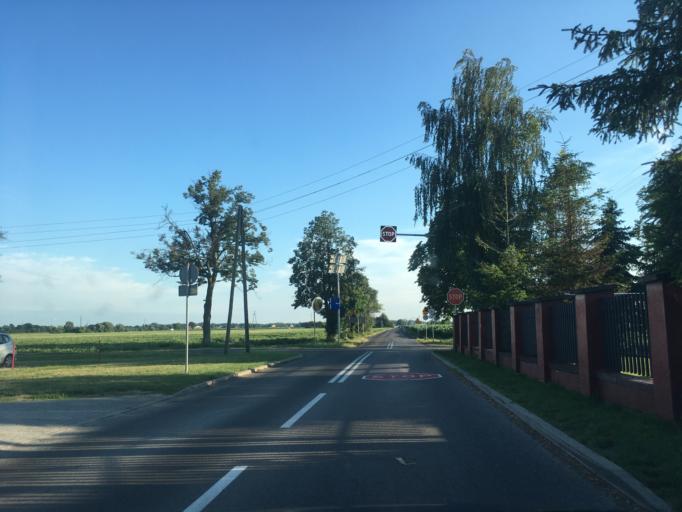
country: PL
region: Masovian Voivodeship
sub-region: Powiat grodziski
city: Grodzisk Mazowiecki
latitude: 52.1321
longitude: 20.5879
